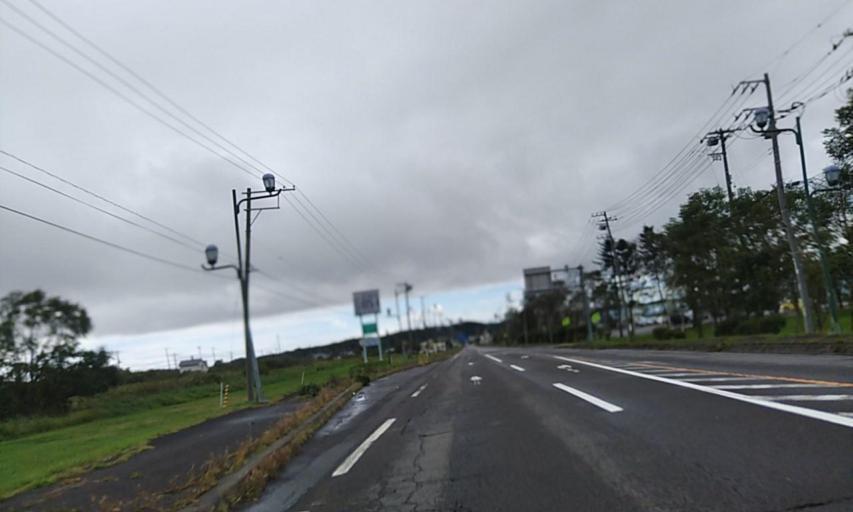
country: JP
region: Hokkaido
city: Kushiro
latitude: 42.8912
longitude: 143.9412
